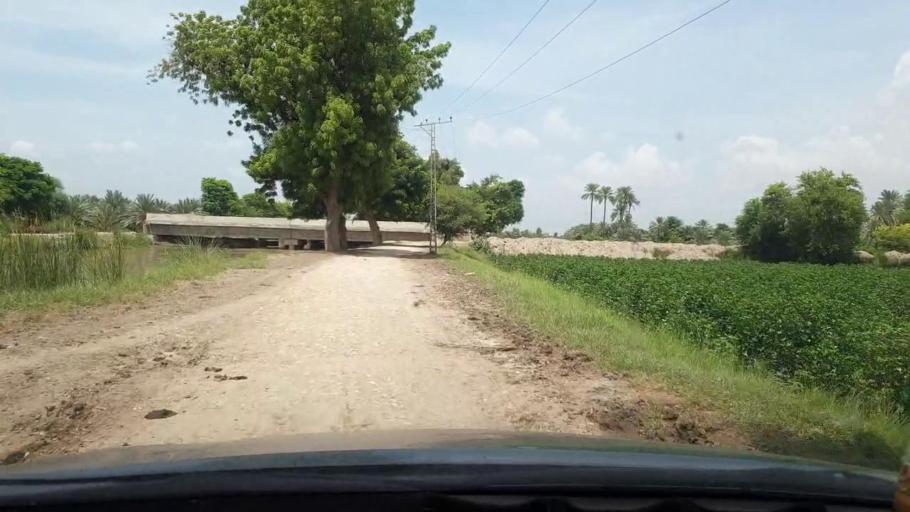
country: PK
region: Sindh
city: Khairpur
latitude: 27.4699
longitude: 68.8067
